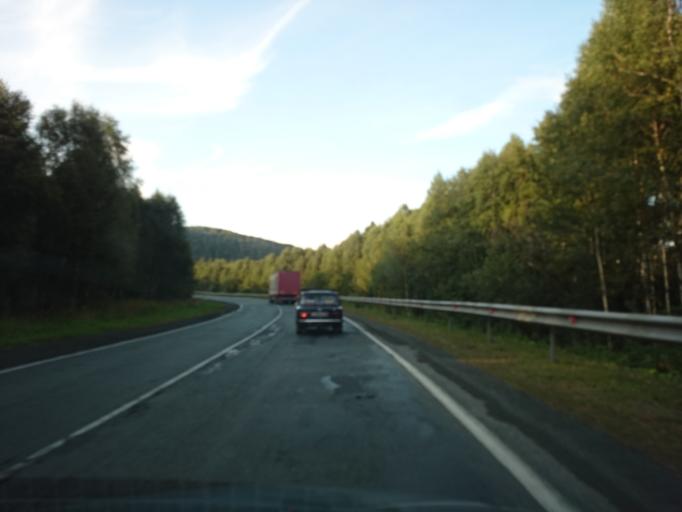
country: RU
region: Bashkortostan
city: Inzer
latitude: 53.9680
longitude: 57.8754
